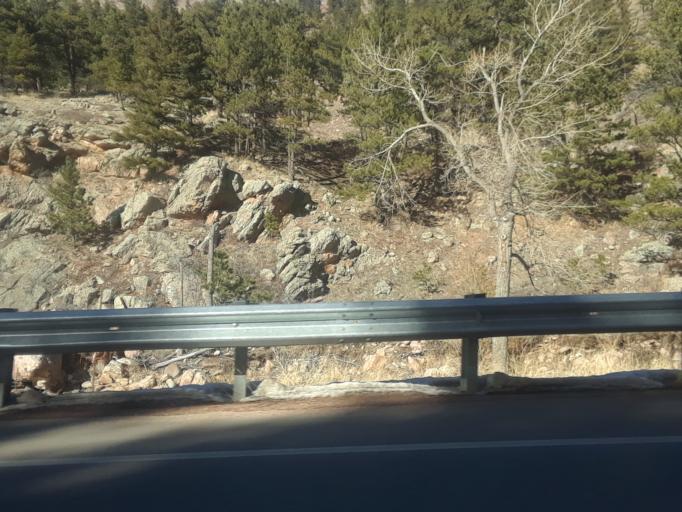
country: US
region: Colorado
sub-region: Boulder County
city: Boulder
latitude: 40.1095
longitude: -105.3165
